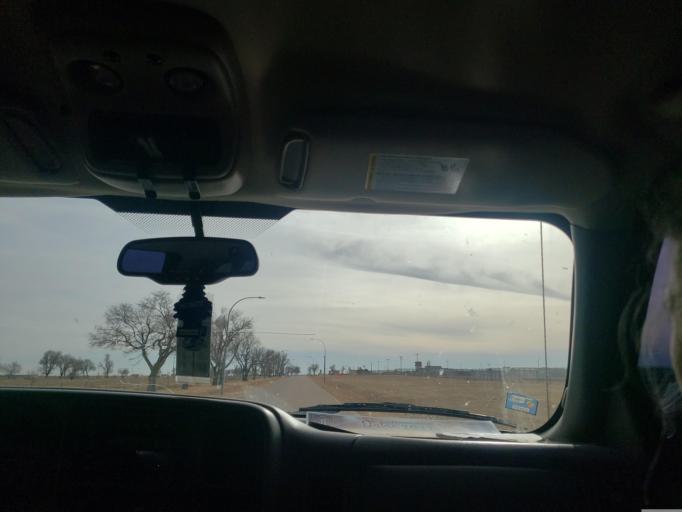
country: US
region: Kansas
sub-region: Finney County
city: Garden City
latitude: 37.9334
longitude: -100.7182
